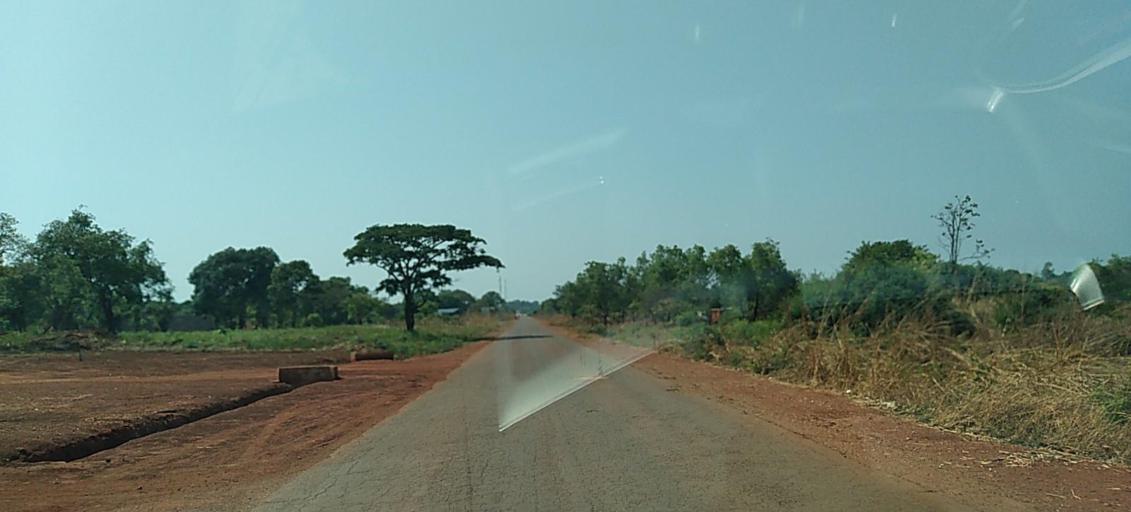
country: ZM
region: North-Western
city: Solwezi
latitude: -12.0970
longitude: 25.4892
